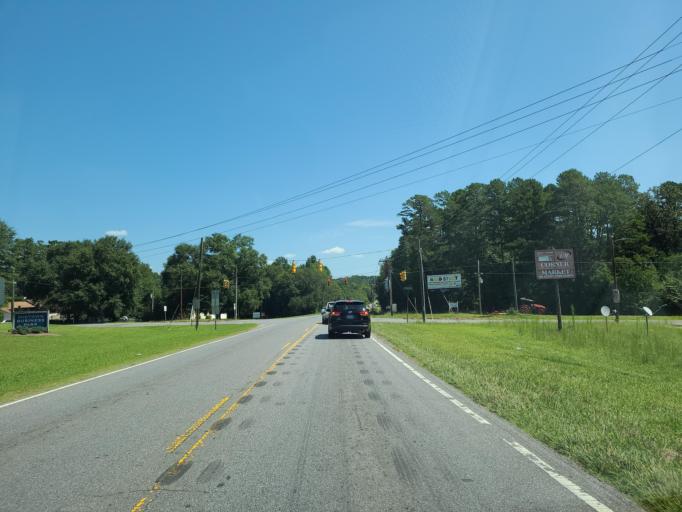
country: US
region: North Carolina
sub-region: Lincoln County
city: Lincolnton
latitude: 35.4438
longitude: -81.2685
